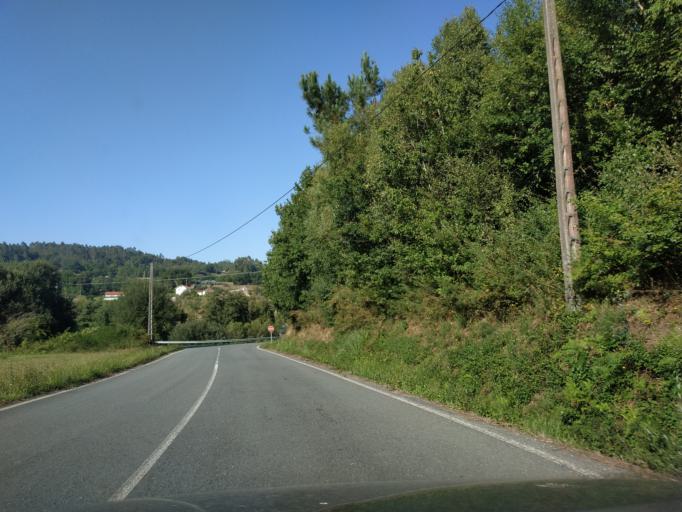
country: ES
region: Galicia
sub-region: Provincia da Coruna
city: Cerceda
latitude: 43.2319
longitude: -8.4890
